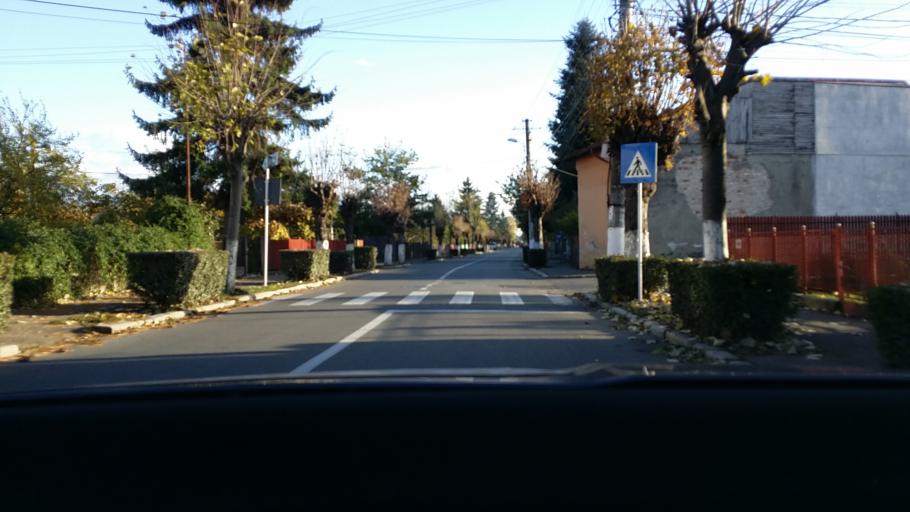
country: RO
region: Prahova
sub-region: Municipiul Campina
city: Campina
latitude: 45.1393
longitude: 25.7355
